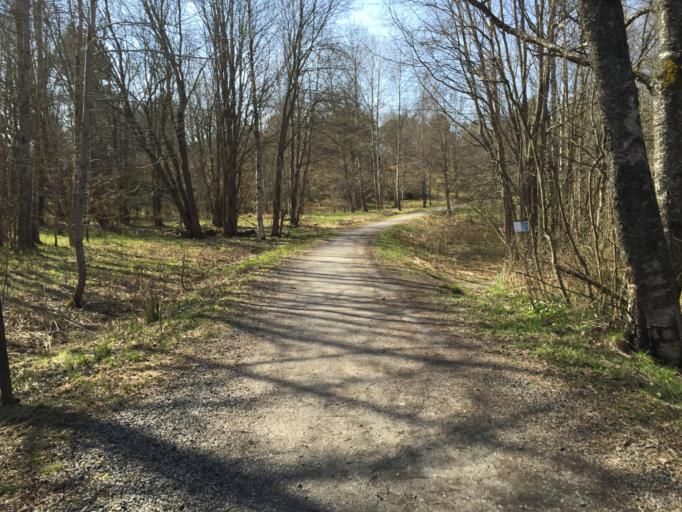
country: SE
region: Stockholm
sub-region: Nacka Kommun
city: Alta
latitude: 59.2699
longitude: 18.1486
